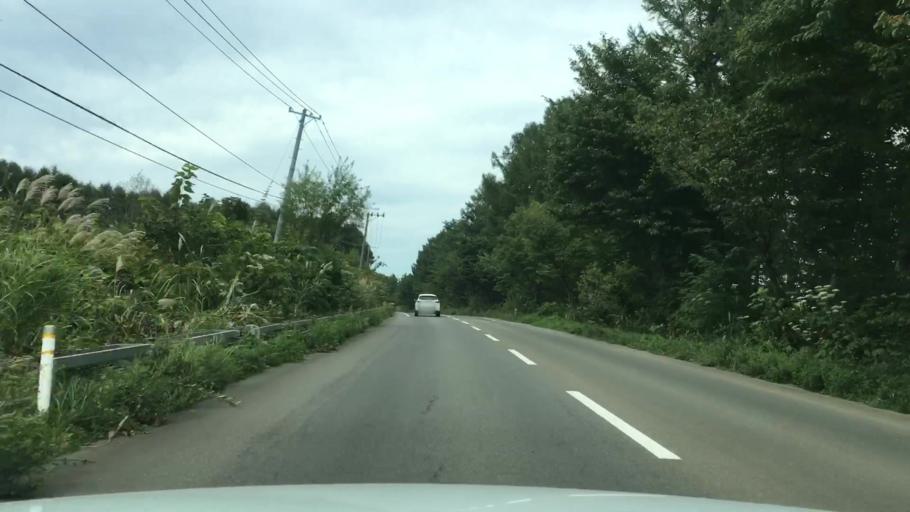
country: JP
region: Aomori
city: Shimokizukuri
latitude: 40.7064
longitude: 140.3423
